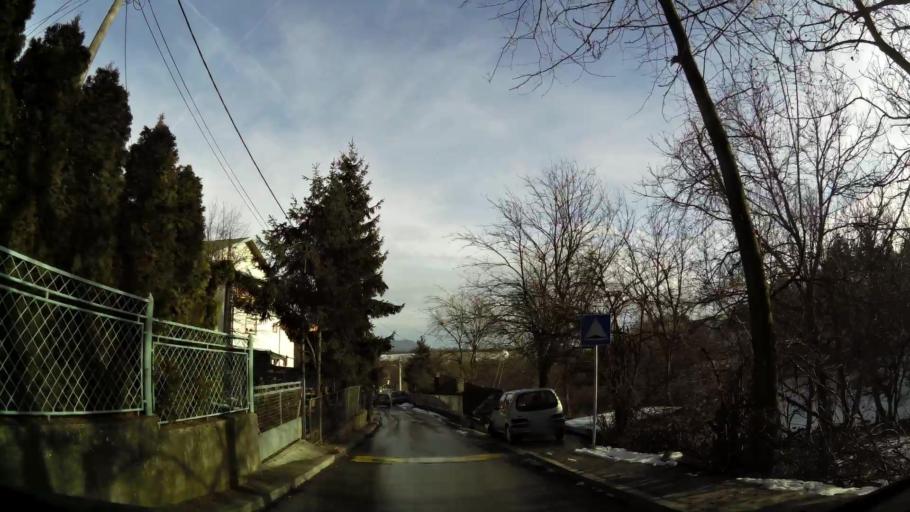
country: RS
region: Central Serbia
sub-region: Belgrade
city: Rakovica
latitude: 44.7219
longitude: 20.4298
